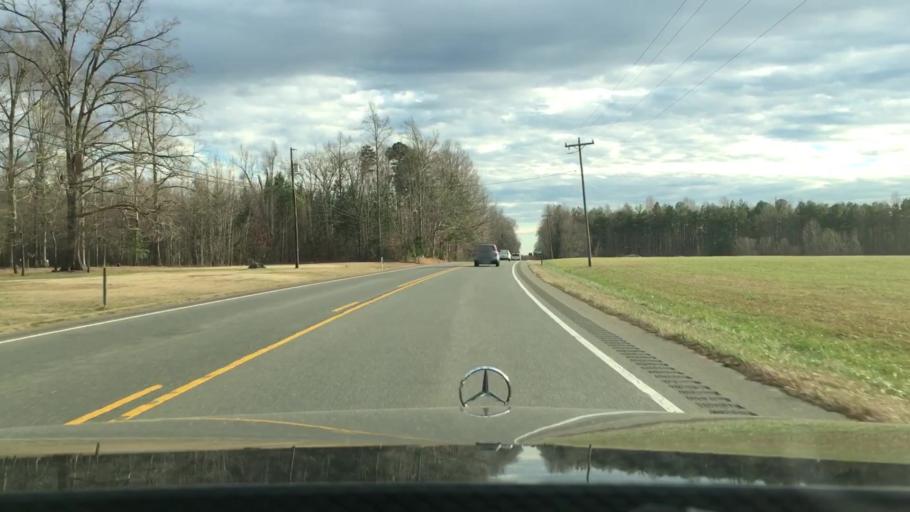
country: US
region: North Carolina
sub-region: Orange County
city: Hillsborough
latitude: 36.1899
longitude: -79.1387
